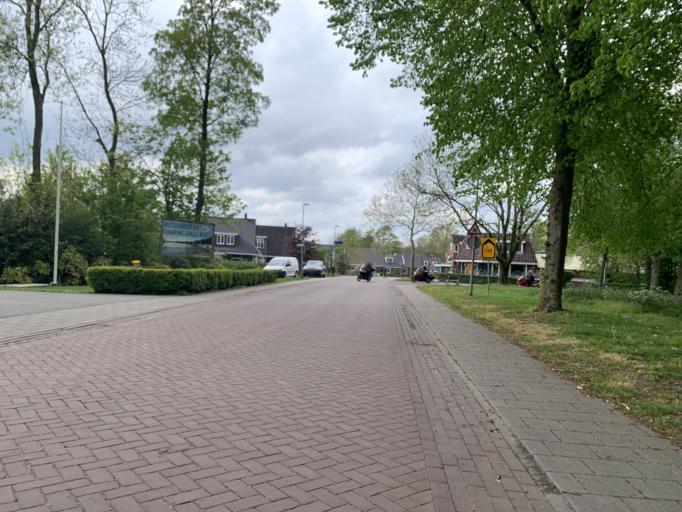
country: NL
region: Groningen
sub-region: Gemeente Haren
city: Haren
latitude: 53.2070
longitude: 6.6489
